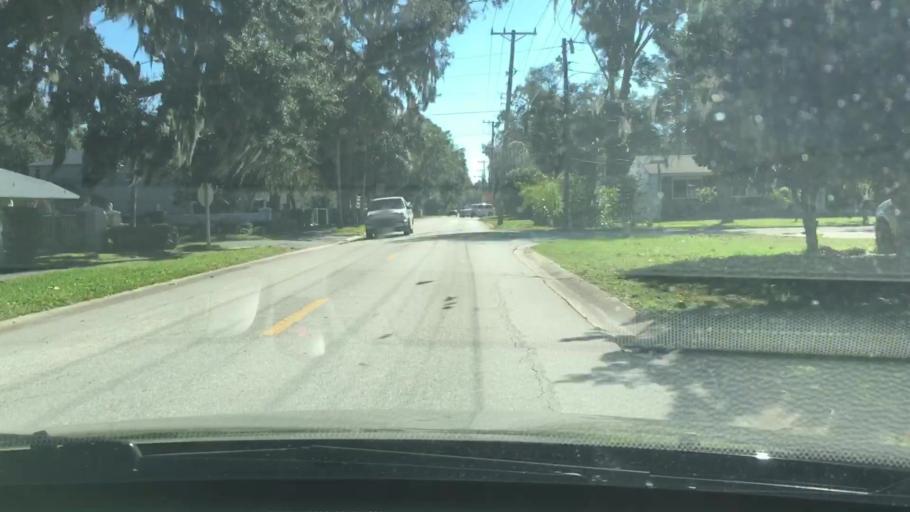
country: US
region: Florida
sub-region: Volusia County
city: Ormond Beach
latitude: 29.2734
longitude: -81.0647
